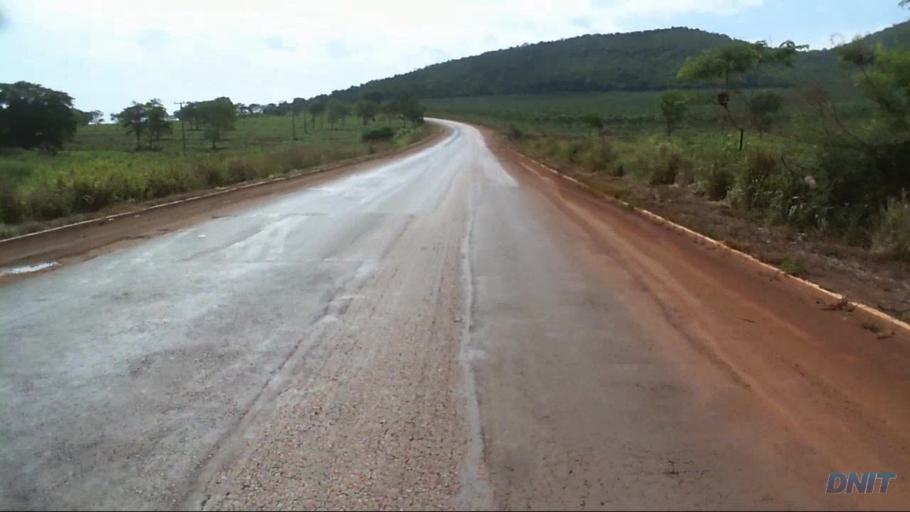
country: BR
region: Goias
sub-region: Barro Alto
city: Barro Alto
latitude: -14.9850
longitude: -48.9234
